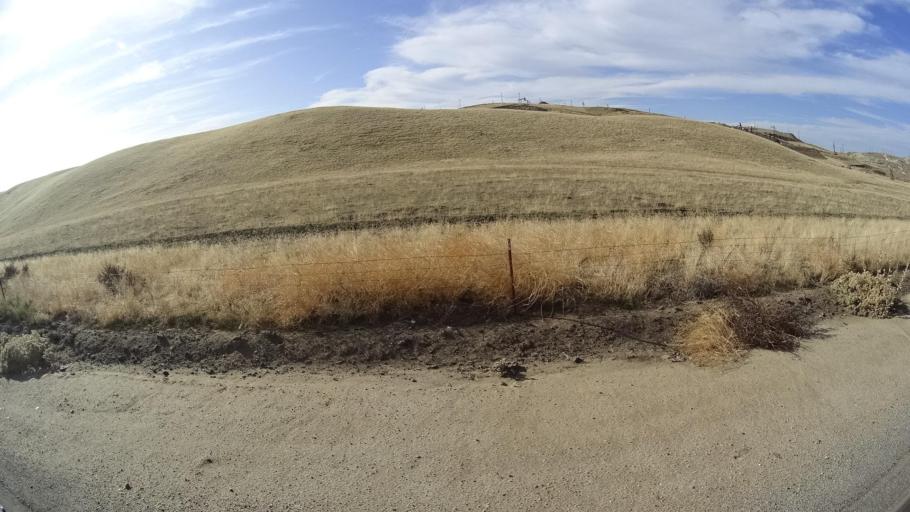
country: US
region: California
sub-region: Kern County
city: Oildale
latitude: 35.6093
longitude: -118.9647
